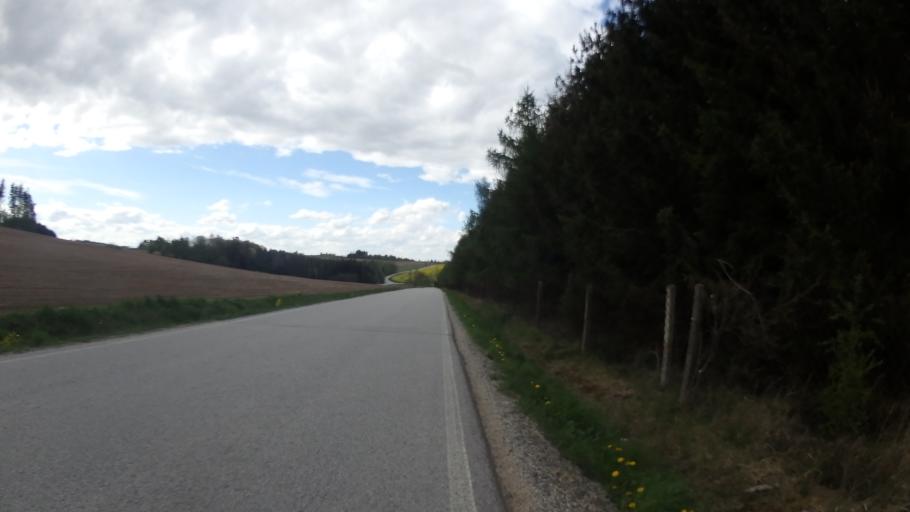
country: CZ
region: Vysocina
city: Merin
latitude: 49.3702
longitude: 15.8965
